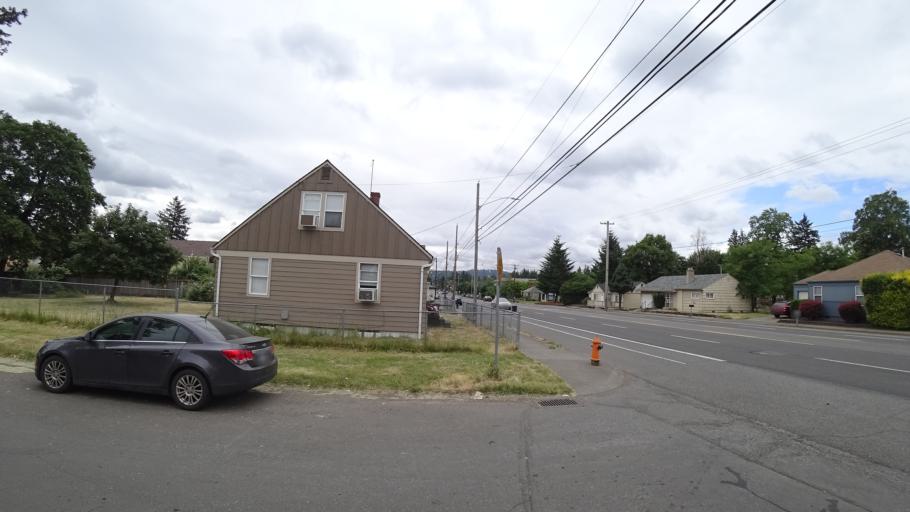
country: US
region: Oregon
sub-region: Multnomah County
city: Lents
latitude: 45.5001
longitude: -122.5375
